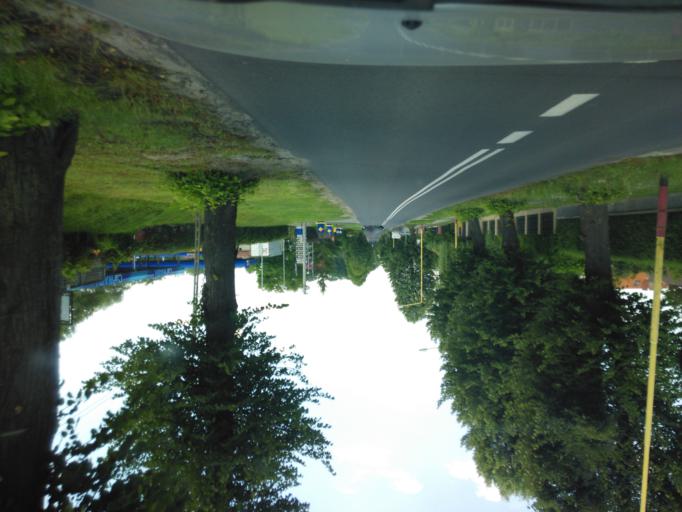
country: PL
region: West Pomeranian Voivodeship
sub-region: Powiat pyrzycki
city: Pyrzyce
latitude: 53.1370
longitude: 14.8985
